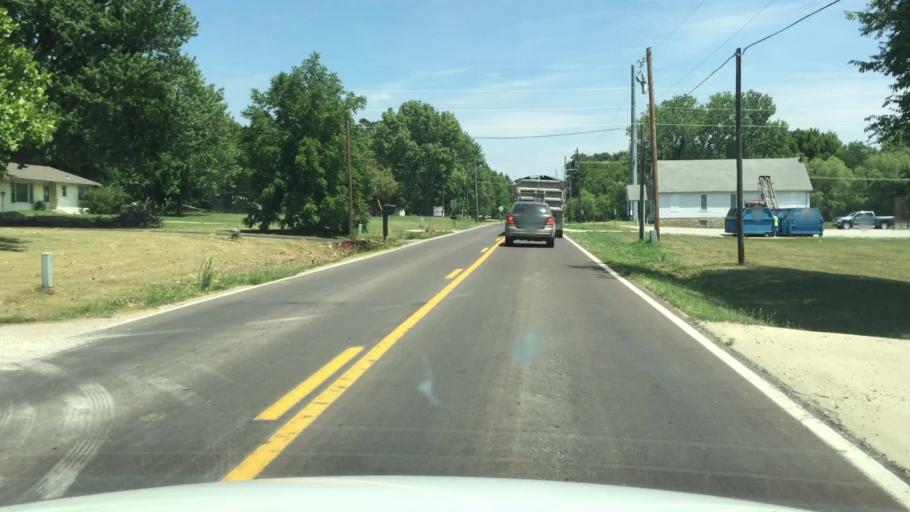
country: US
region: Kansas
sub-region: Shawnee County
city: Topeka
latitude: 38.9861
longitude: -95.5583
